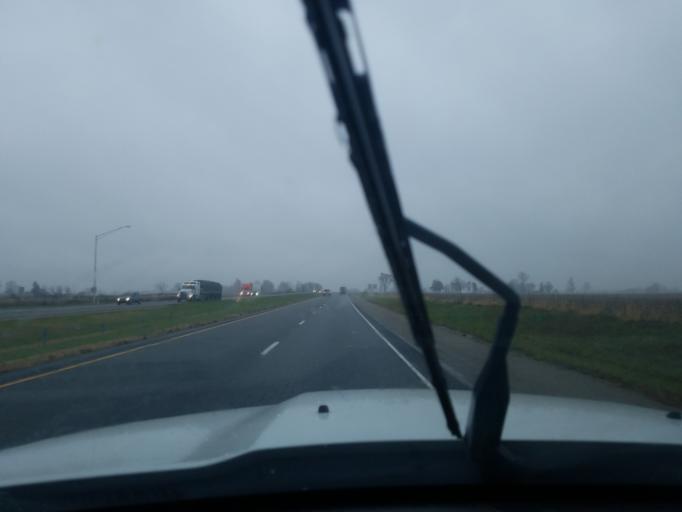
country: US
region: Indiana
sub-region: Grant County
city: Fairmount
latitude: 40.3469
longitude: -85.5589
